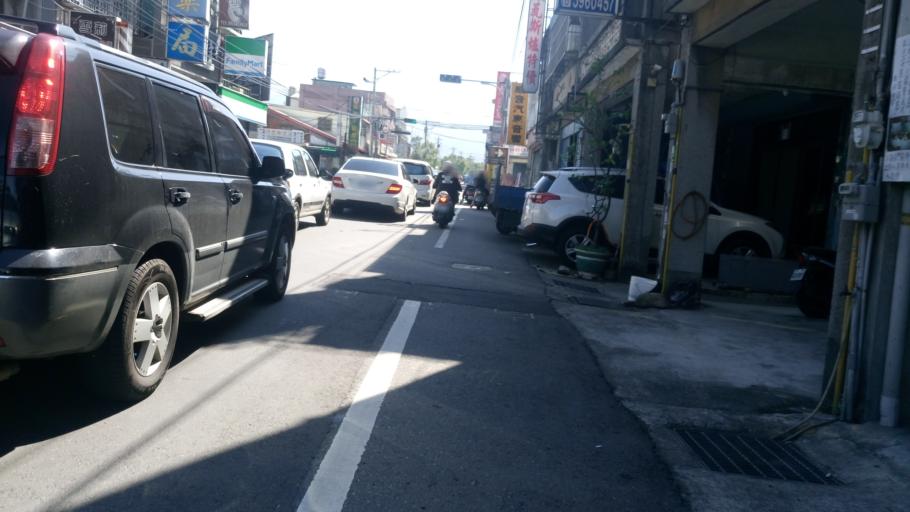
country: TW
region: Taiwan
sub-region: Hsinchu
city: Zhubei
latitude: 24.7299
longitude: 121.0914
